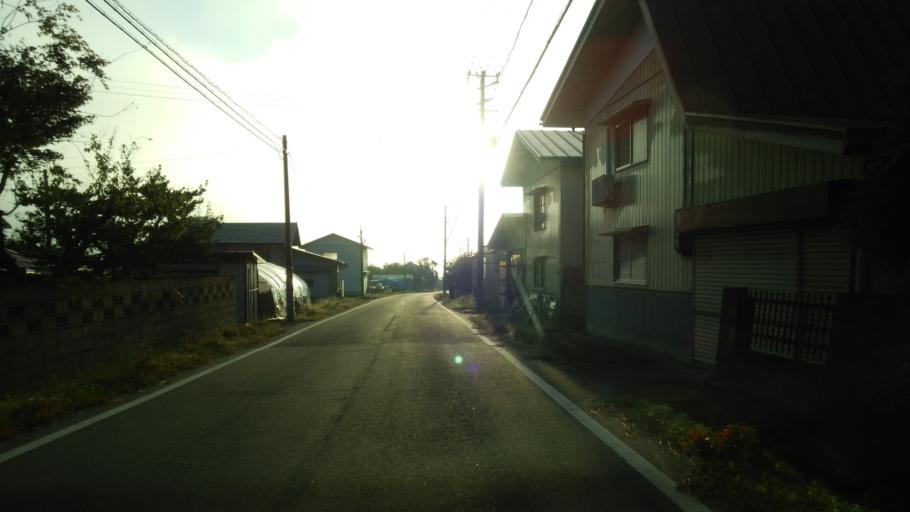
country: JP
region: Fukushima
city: Kitakata
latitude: 37.4446
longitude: 139.8121
